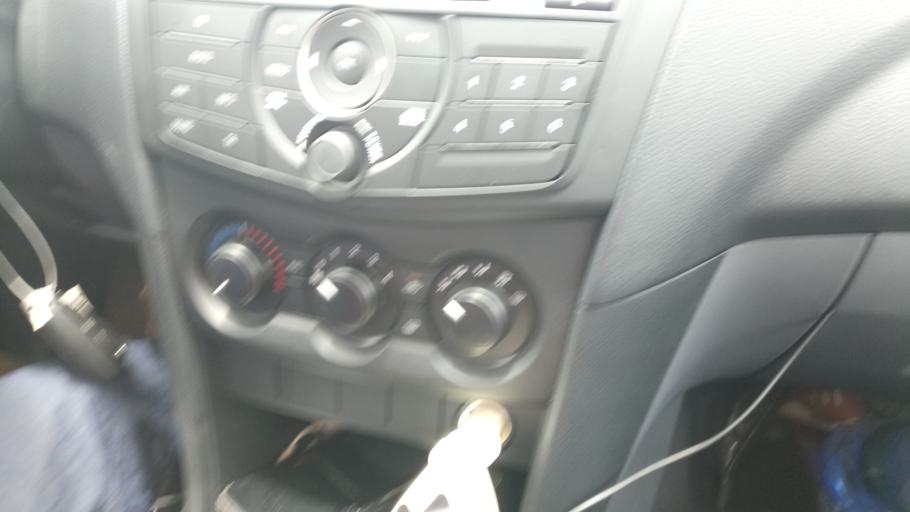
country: CD
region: Katanga
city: Lubumbashi
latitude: -11.5706
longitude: 27.5463
